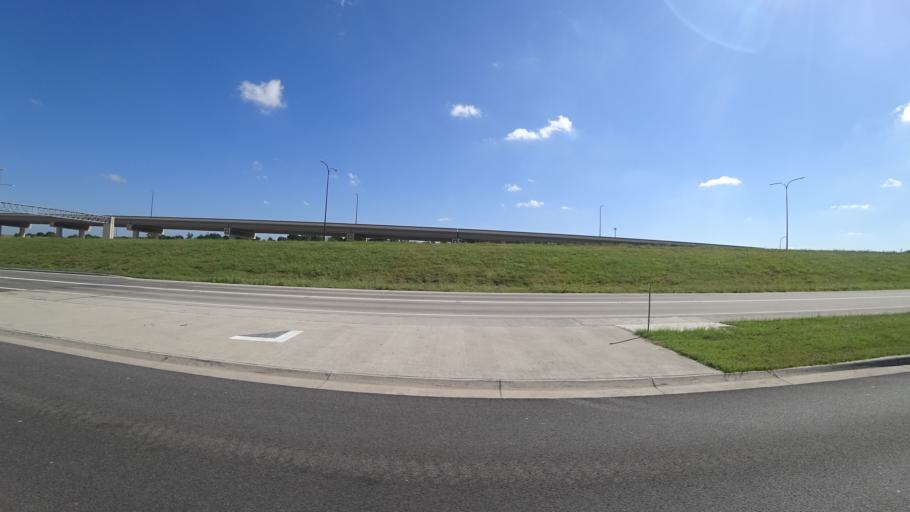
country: US
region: Texas
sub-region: Travis County
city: Manor
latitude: 30.3380
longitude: -97.5995
